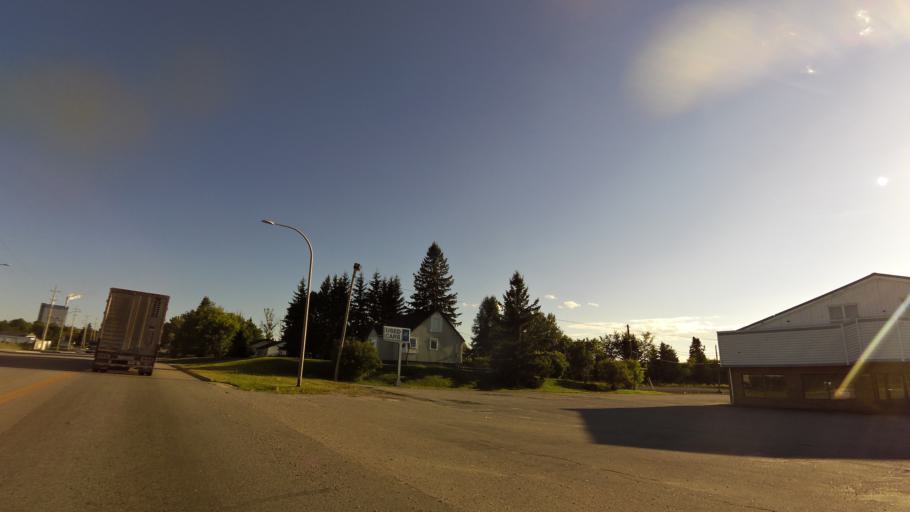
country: CA
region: Ontario
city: Dryden
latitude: 49.7941
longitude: -92.8474
